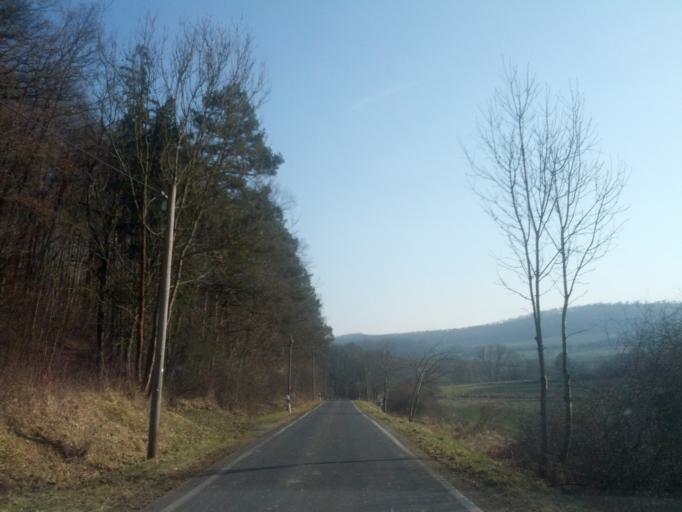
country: DE
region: Thuringia
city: Ifta
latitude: 51.0747
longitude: 10.1619
